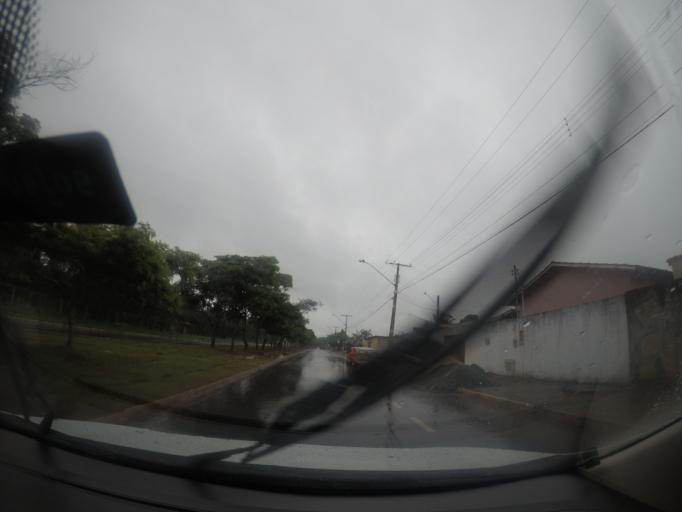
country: BR
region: Goias
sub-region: Goiania
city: Goiania
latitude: -16.5980
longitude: -49.3387
